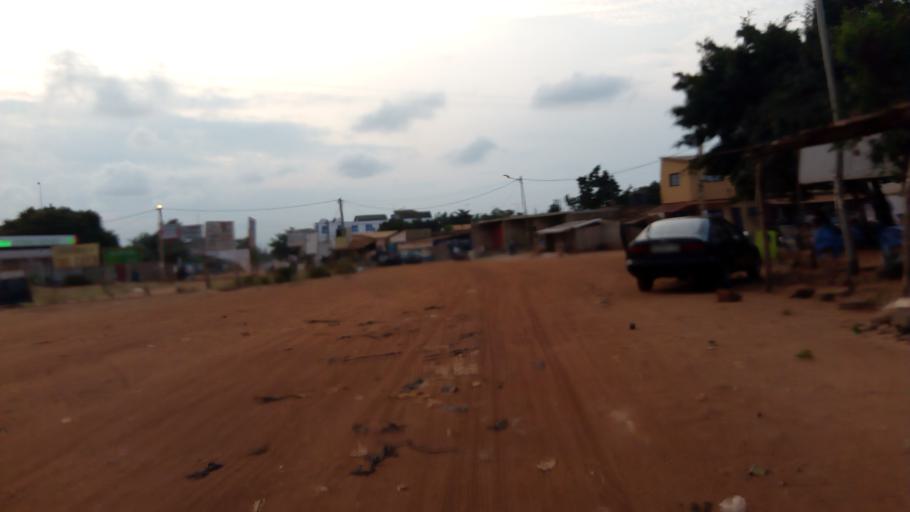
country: TG
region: Maritime
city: Lome
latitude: 6.2329
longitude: 1.1897
